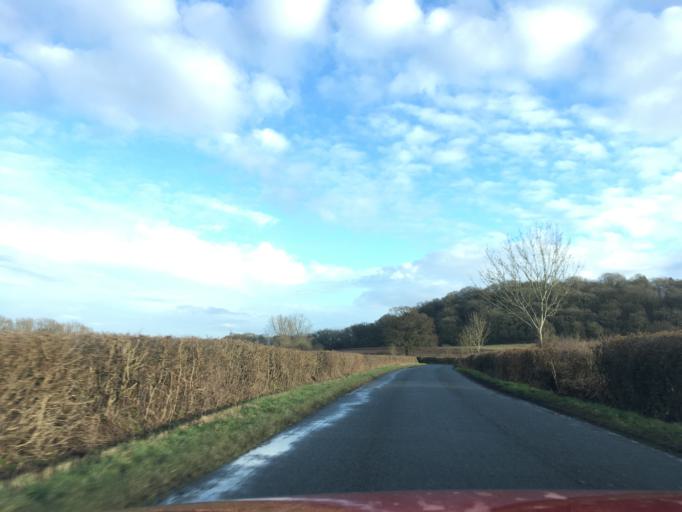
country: GB
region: England
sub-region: Warwickshire
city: Alcester
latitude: 52.2234
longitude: -1.8029
